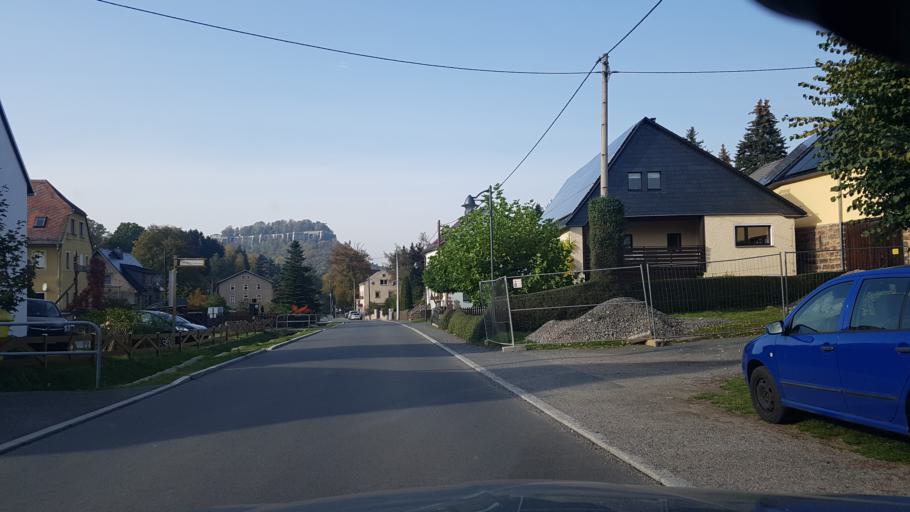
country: DE
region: Saxony
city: Konigstein
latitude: 50.9091
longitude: 14.0783
